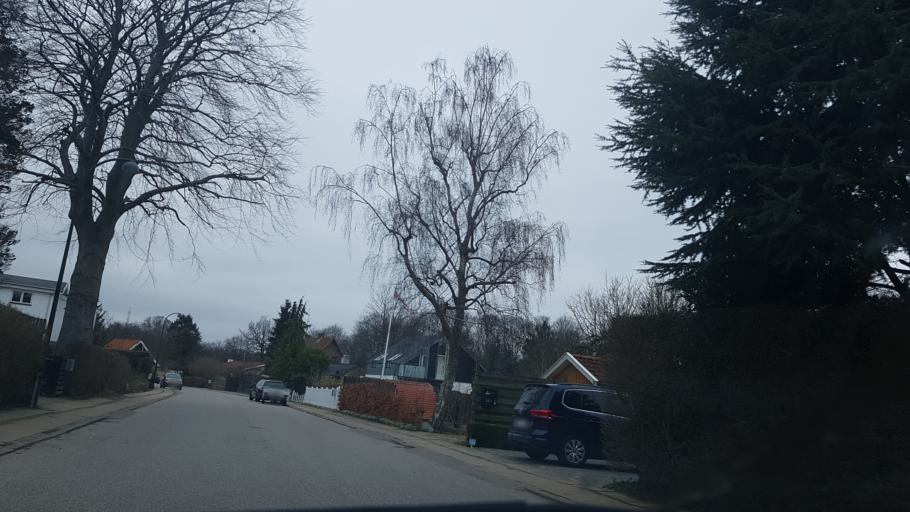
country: DK
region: Capital Region
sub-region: Lyngby-Tarbaek Kommune
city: Kongens Lyngby
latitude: 55.7513
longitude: 12.5079
